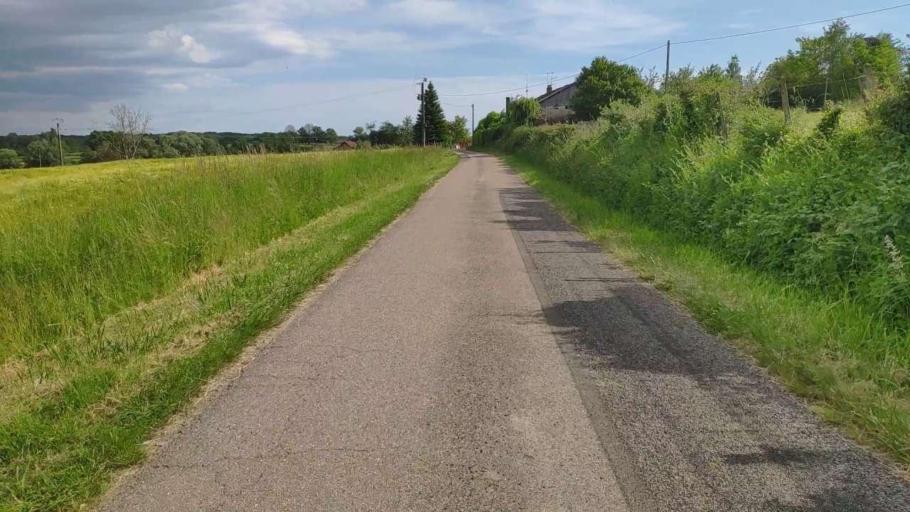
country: FR
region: Bourgogne
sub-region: Departement de Saone-et-Loire
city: Saint-Germain-du-Bois
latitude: 46.8074
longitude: 5.3405
